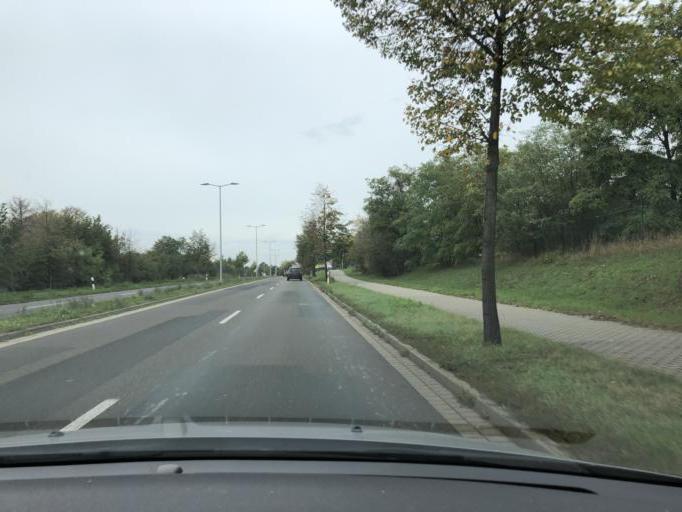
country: DE
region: Saxony
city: Schkeuditz
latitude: 51.4031
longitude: 12.2188
